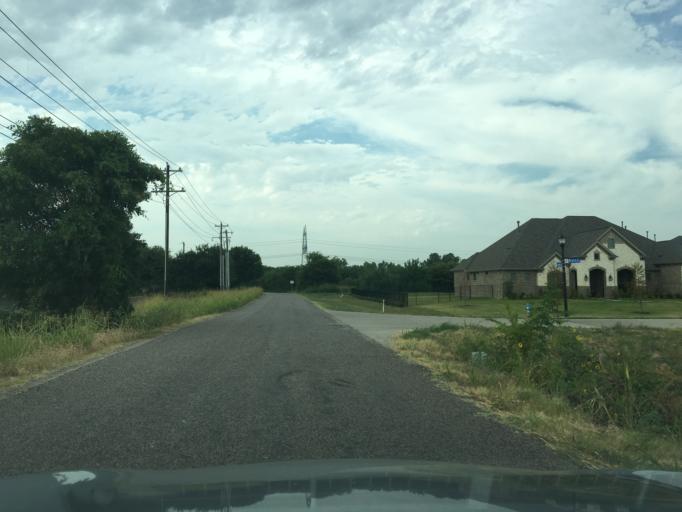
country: US
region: Texas
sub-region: Collin County
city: Parker
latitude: 33.0639
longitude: -96.6013
